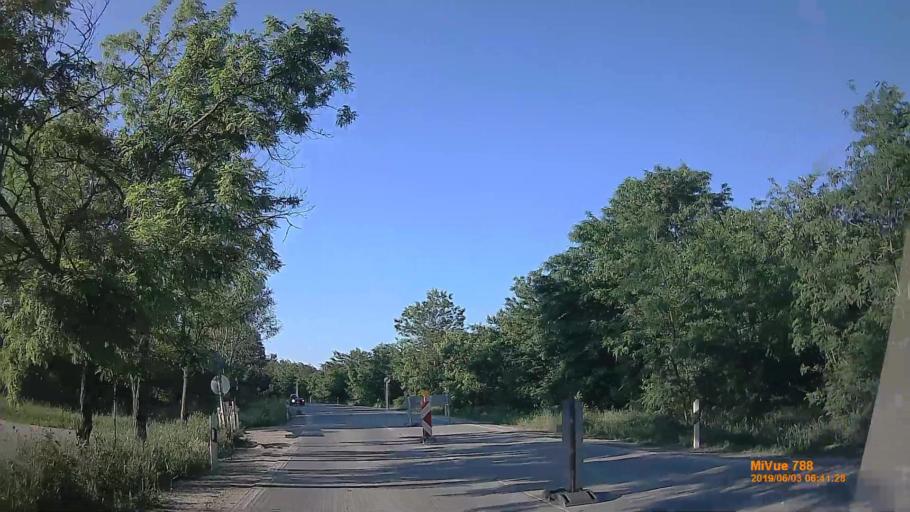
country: HU
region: Pest
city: Delegyhaza
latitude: 47.2755
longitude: 19.1066
